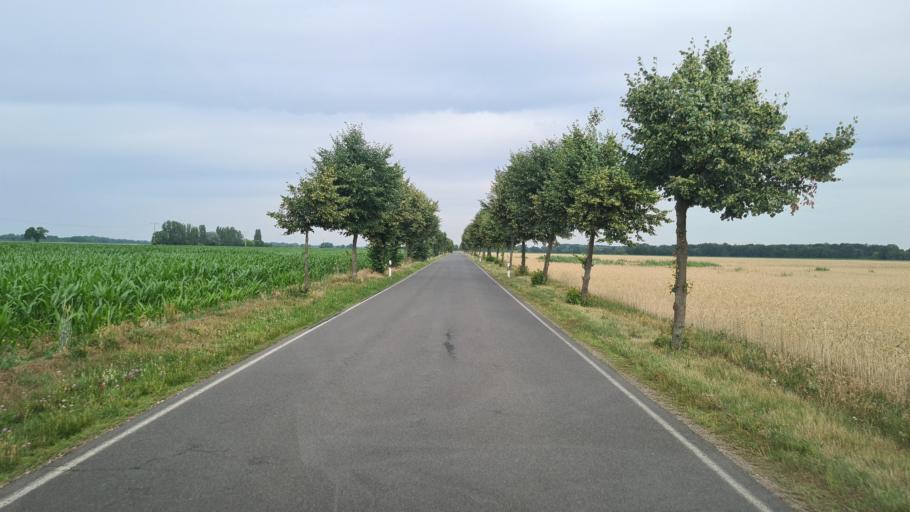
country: DE
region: Saxony-Anhalt
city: Jessen
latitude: 51.7843
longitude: 12.9127
